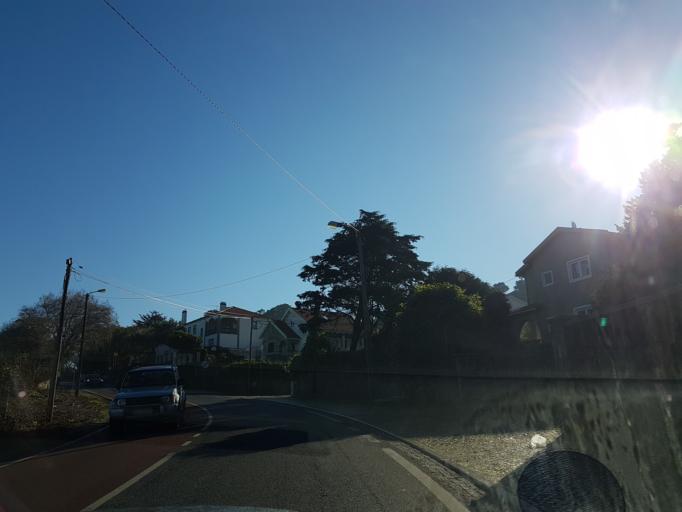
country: PT
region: Lisbon
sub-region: Sintra
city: Sintra
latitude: 38.7960
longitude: -9.3778
